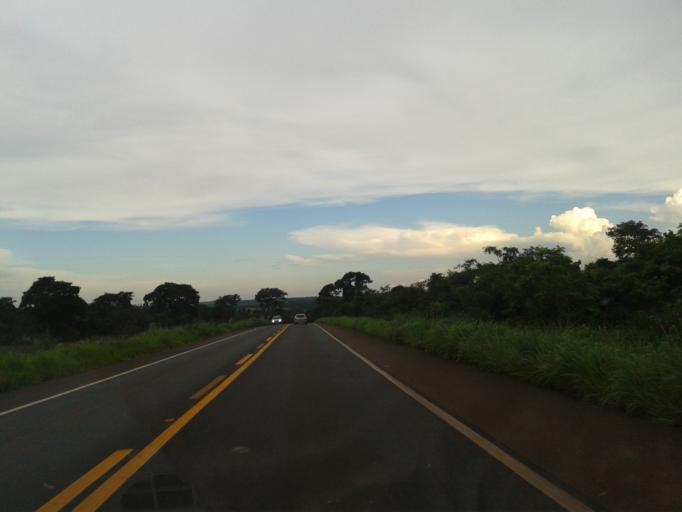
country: BR
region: Minas Gerais
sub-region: Santa Vitoria
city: Santa Vitoria
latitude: -18.8798
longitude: -50.1326
